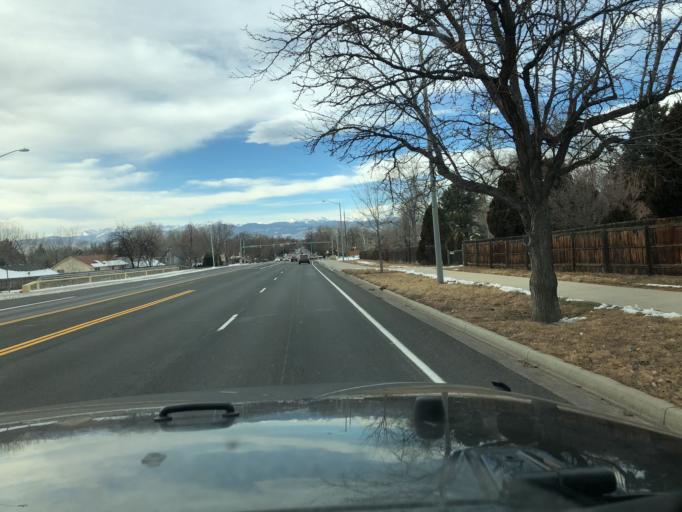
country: US
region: Colorado
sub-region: Boulder County
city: Longmont
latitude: 40.1741
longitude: -105.0805
